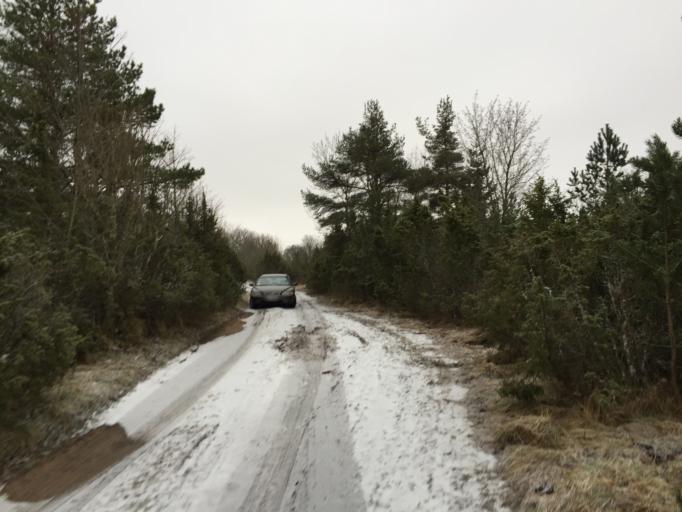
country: EE
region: Saare
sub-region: Orissaare vald
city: Orissaare
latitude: 58.6056
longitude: 23.1145
